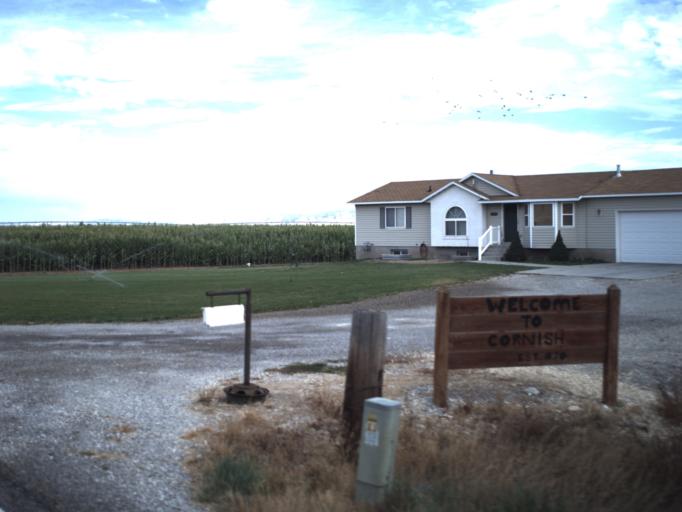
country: US
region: Utah
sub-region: Cache County
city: Lewiston
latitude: 41.9433
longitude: -111.9537
